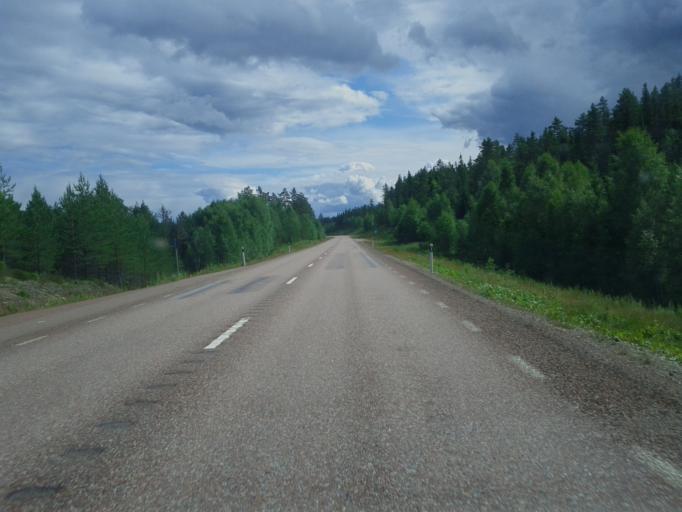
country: SE
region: Dalarna
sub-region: Rattviks Kommun
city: Raettvik
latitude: 60.8077
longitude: 15.2623
